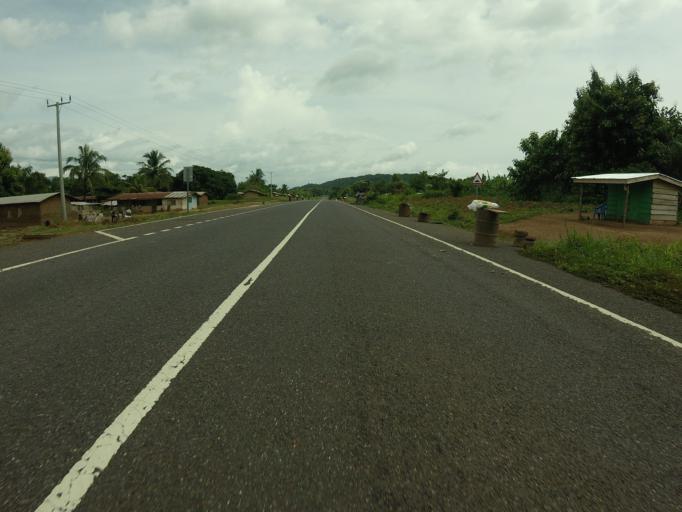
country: TG
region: Plateaux
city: Badou
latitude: 7.9540
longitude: 0.5546
